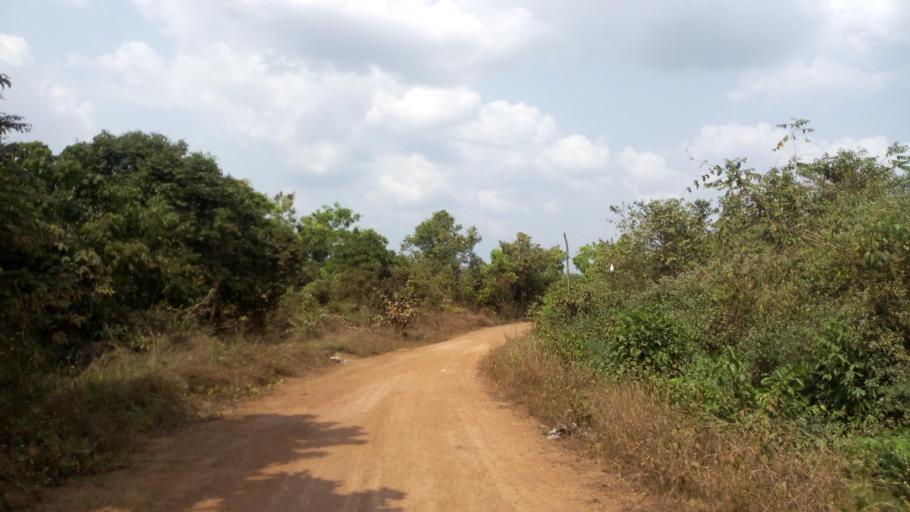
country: SL
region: Southern Province
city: Mogbwemo
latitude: 7.7939
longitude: -12.3075
